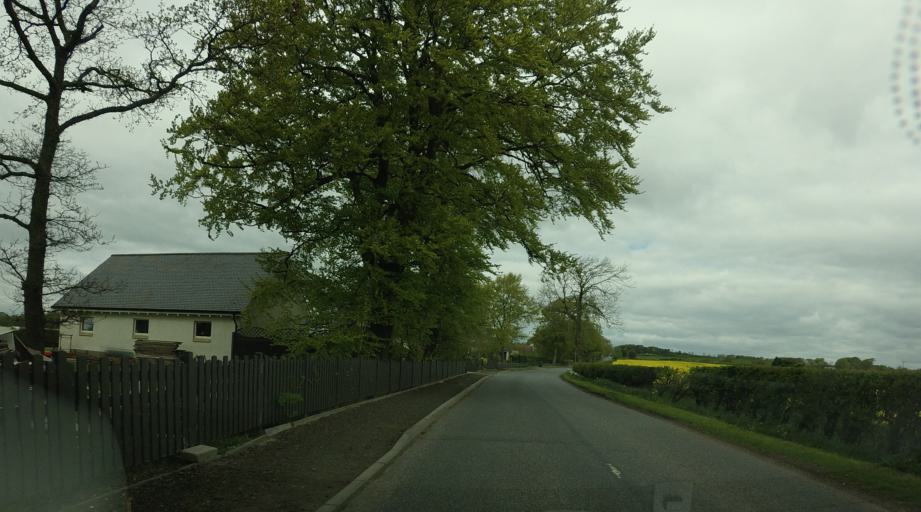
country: GB
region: Scotland
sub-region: Perth and Kinross
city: Milnathort
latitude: 56.2414
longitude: -3.3716
